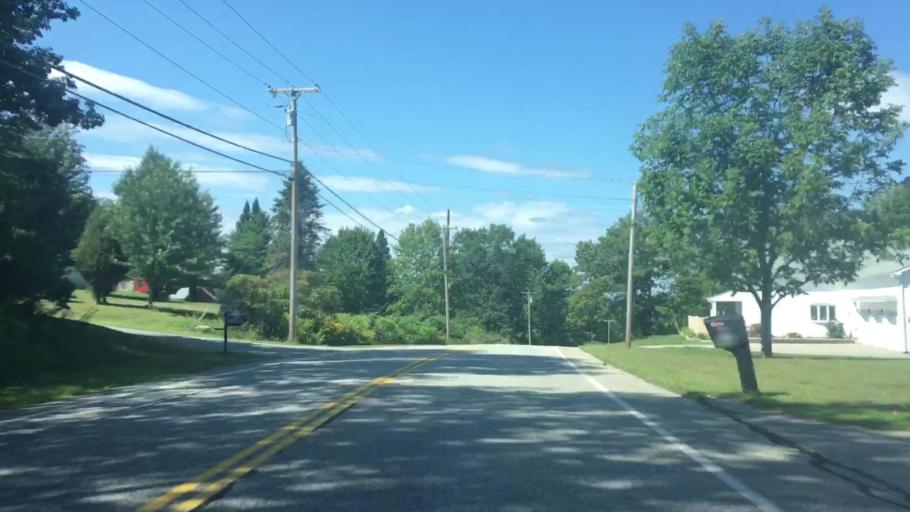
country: US
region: Maine
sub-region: Androscoggin County
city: Sabattus
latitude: 44.0863
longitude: -70.1394
